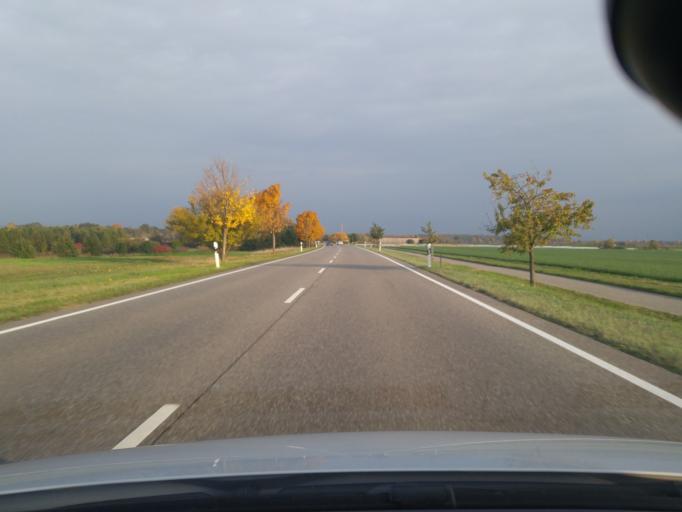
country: DE
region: Baden-Wuerttemberg
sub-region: Karlsruhe Region
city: Neulussheim
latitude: 49.3065
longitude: 8.5146
